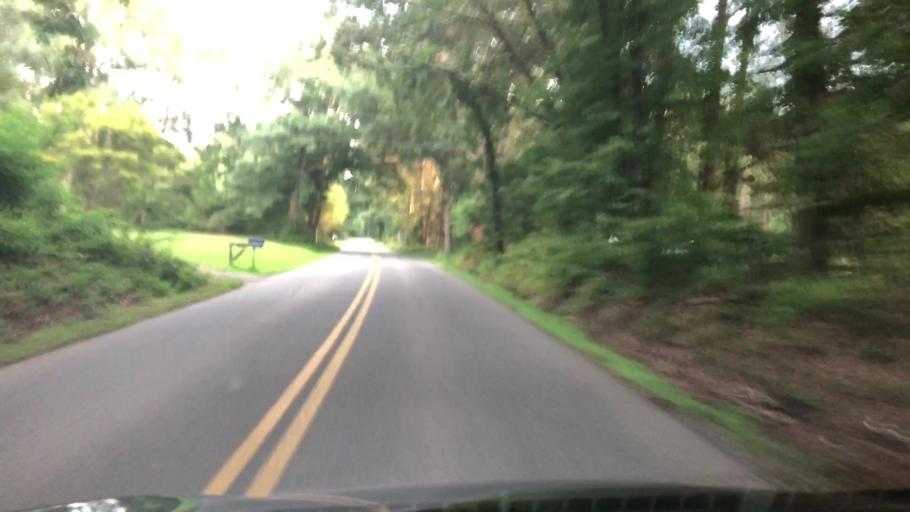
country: US
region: Virginia
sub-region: Fauquier County
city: Bealeton
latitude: 38.5373
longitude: -77.6735
